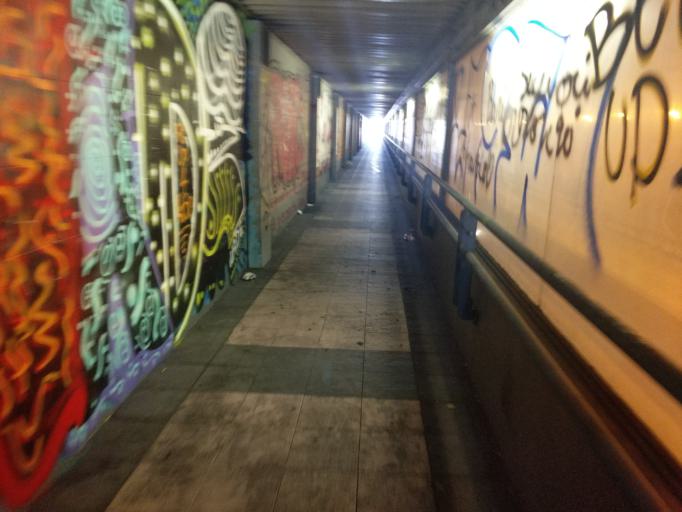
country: IT
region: Apulia
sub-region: Provincia di Bari
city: Bari
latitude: 41.1174
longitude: 16.8524
